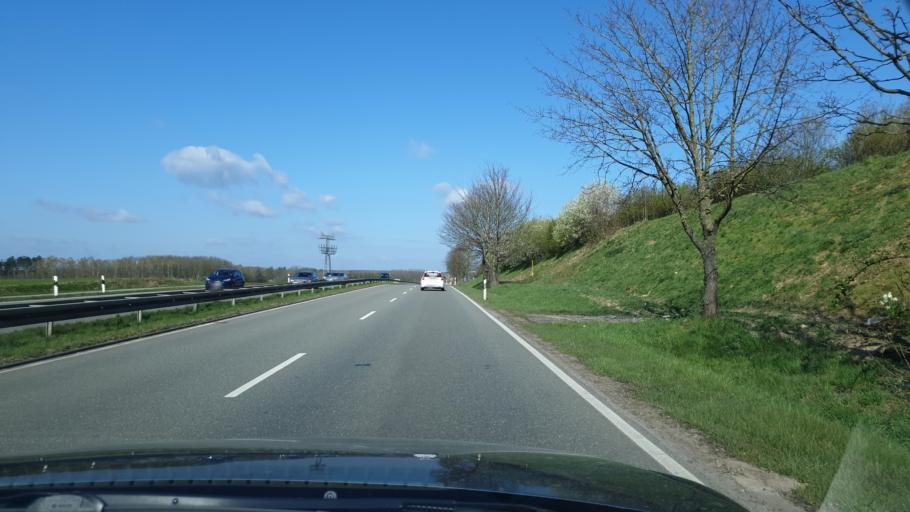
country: DE
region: Mecklenburg-Vorpommern
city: Neumuehle
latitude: 53.6346
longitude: 11.3589
